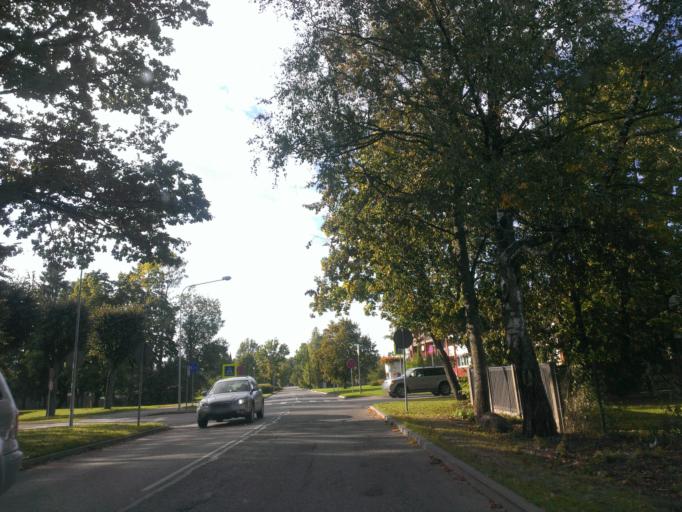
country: LV
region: Sigulda
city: Sigulda
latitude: 57.1604
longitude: 24.8616
